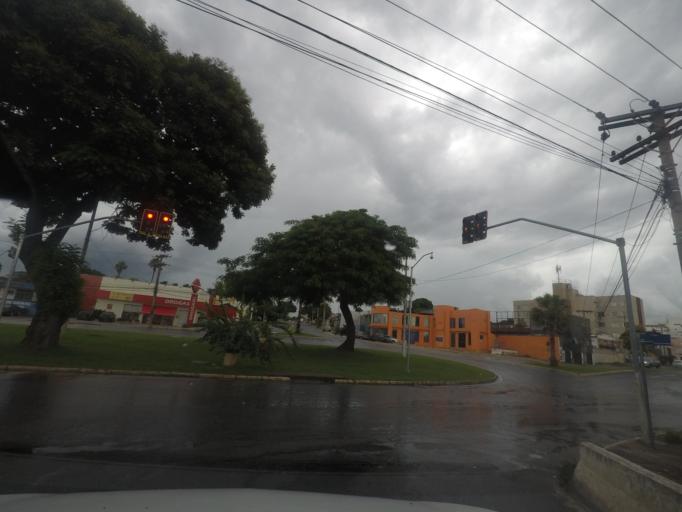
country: BR
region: Goias
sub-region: Goiania
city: Goiania
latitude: -16.6856
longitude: -49.2466
